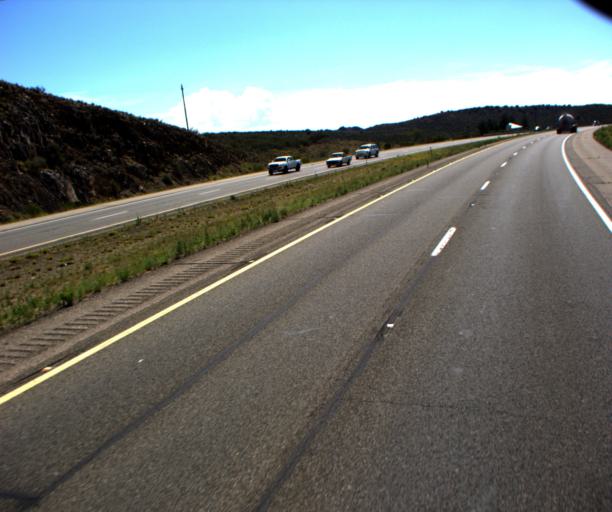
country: US
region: Arizona
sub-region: Yavapai County
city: Mayer
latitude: 34.3979
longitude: -112.2265
